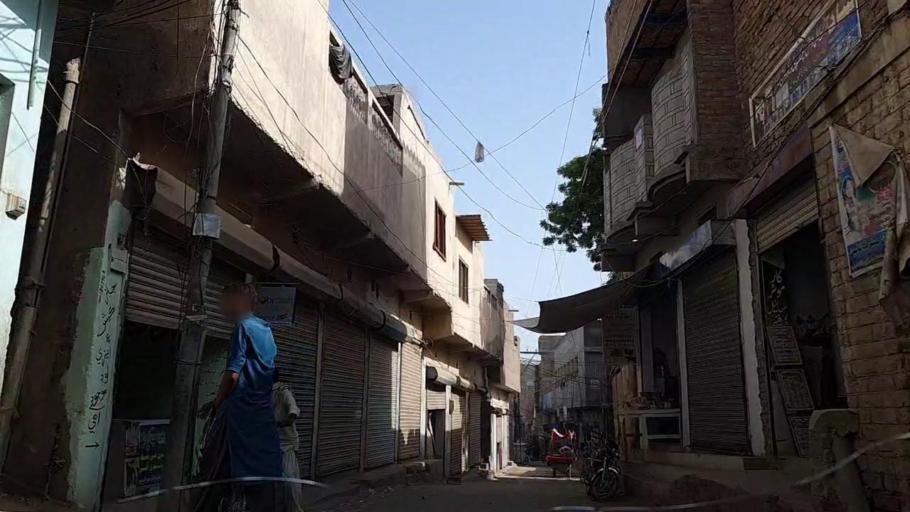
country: PK
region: Sindh
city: Kandiaro
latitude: 27.0611
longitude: 68.2078
